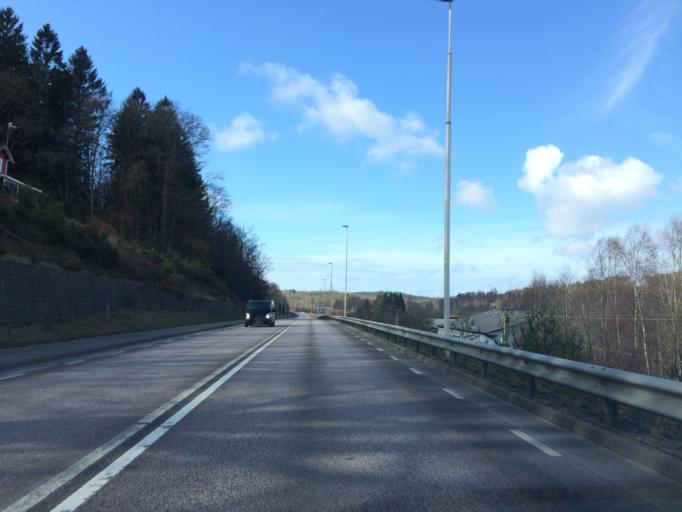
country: SE
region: Halland
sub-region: Laholms Kommun
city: Knared
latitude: 56.5141
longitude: 13.3158
